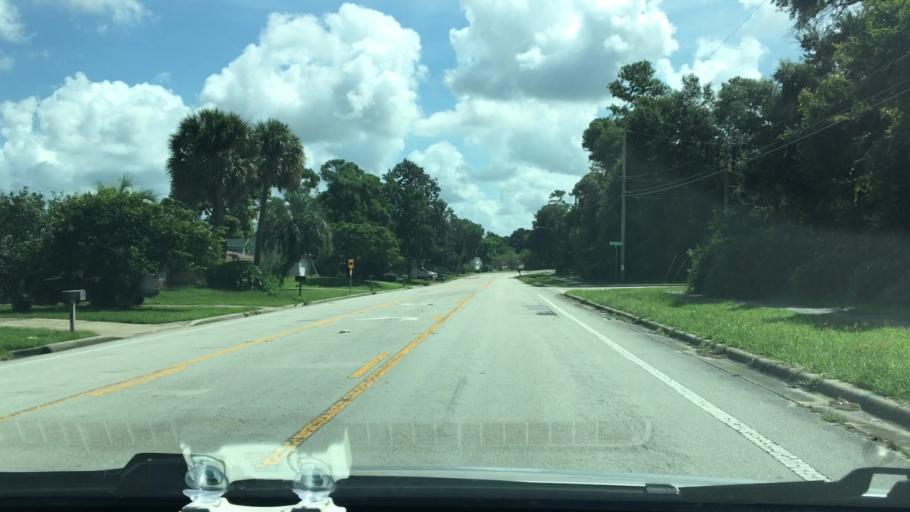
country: US
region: Florida
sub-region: Volusia County
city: Deltona
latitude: 28.8827
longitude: -81.2270
